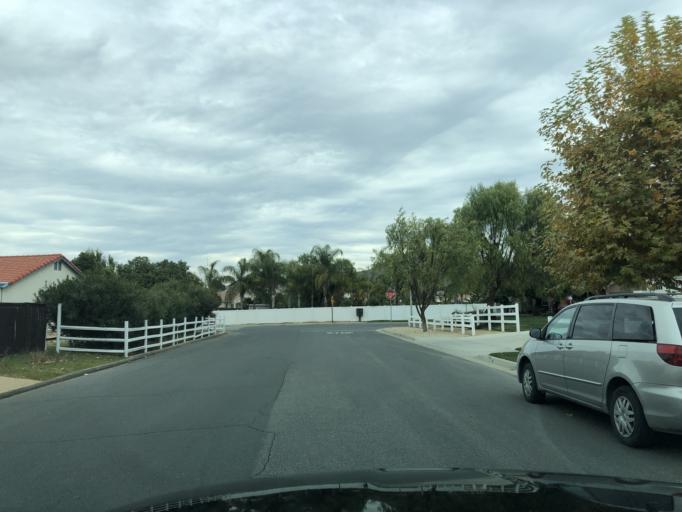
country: US
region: California
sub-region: Riverside County
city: Wildomar
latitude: 33.6147
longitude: -117.2797
